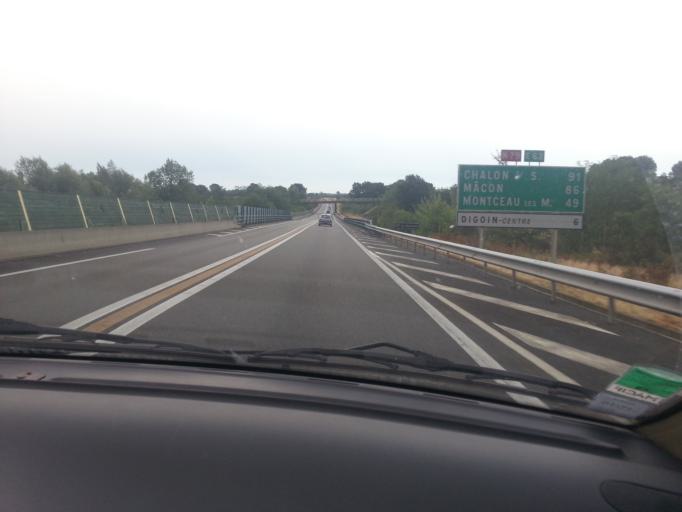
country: FR
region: Auvergne
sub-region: Departement de l'Allier
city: Molinet
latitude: 46.4567
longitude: 3.9289
